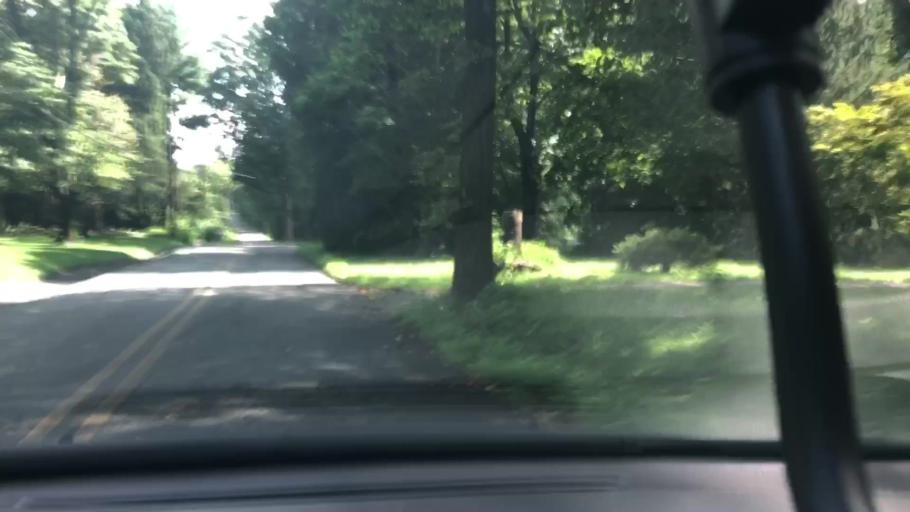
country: US
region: Pennsylvania
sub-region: Chester County
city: Kenilworth
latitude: 40.2045
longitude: -75.6338
